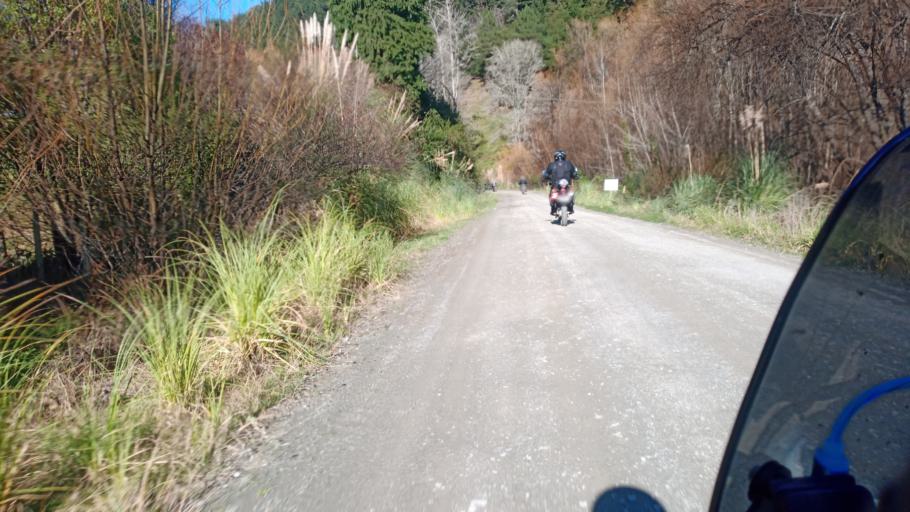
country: NZ
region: Gisborne
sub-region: Gisborne District
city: Gisborne
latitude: -38.2845
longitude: 177.8509
